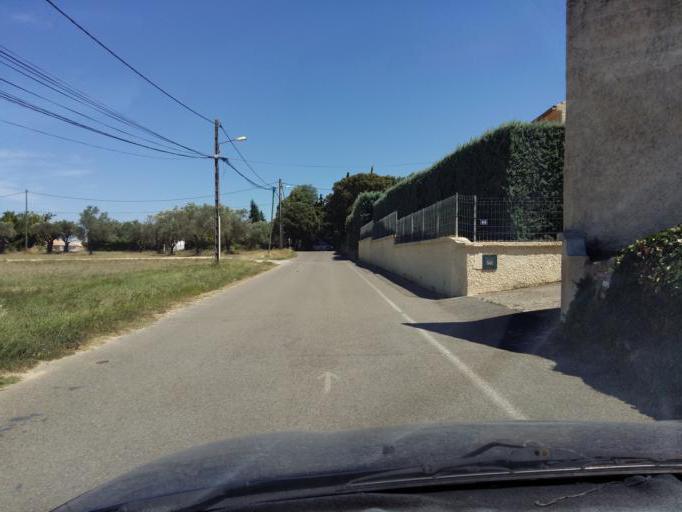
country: FR
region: Provence-Alpes-Cote d'Azur
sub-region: Departement du Vaucluse
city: Piolenc
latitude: 44.1759
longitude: 4.7700
